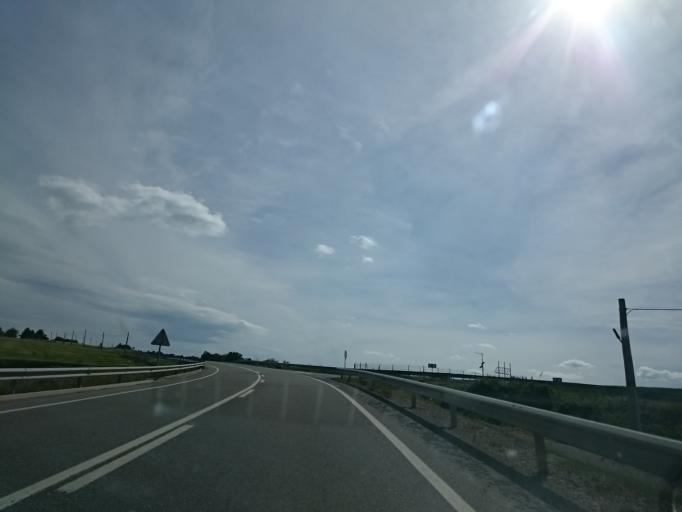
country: ES
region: Catalonia
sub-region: Provincia de Lleida
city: Sant Guim de Freixenet
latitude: 41.6132
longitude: 1.4002
